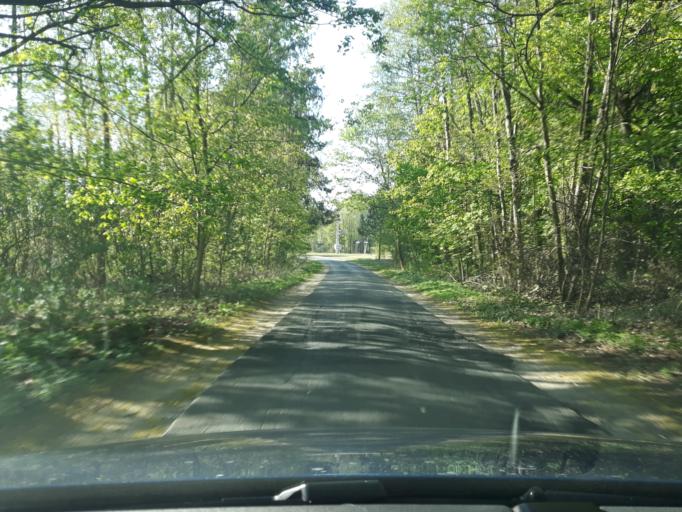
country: PL
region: Pomeranian Voivodeship
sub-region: Powiat czluchowski
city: Przechlewo
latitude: 53.8749
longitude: 17.3301
